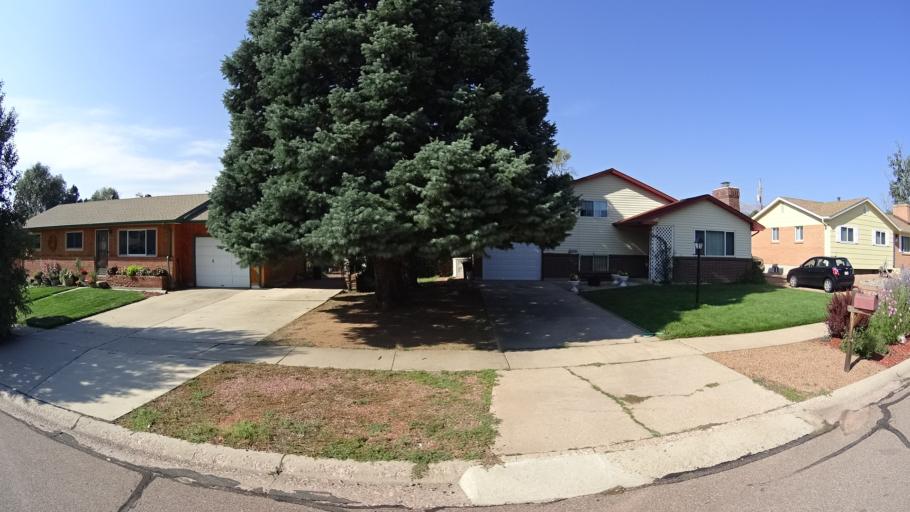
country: US
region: Colorado
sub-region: El Paso County
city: Colorado Springs
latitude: 38.8883
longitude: -104.8375
